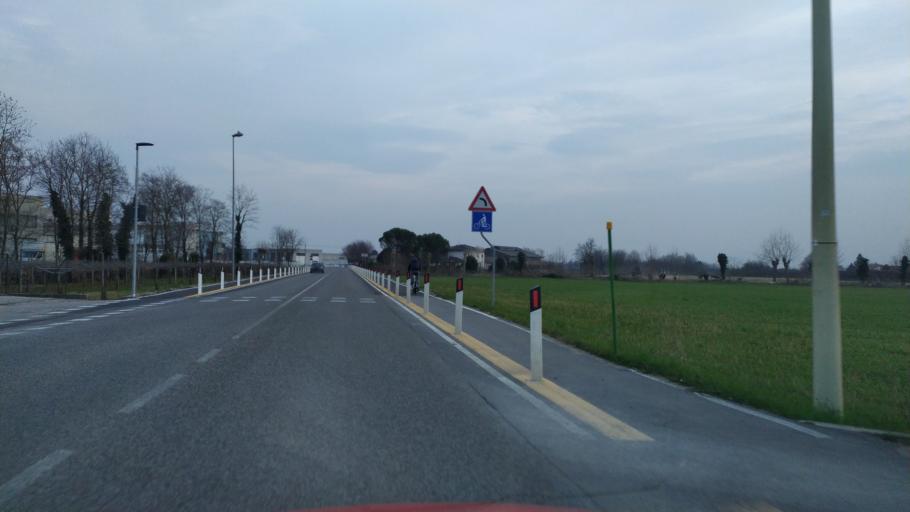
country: IT
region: Veneto
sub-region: Provincia di Vicenza
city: Dueville
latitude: 45.6275
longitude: 11.5637
